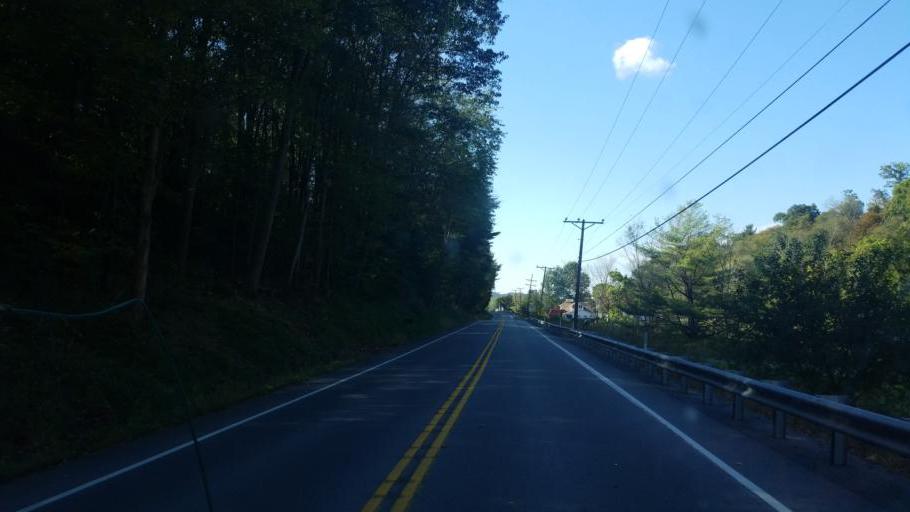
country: US
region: Pennsylvania
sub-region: Blair County
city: Claysburg
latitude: 40.1761
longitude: -78.5142
